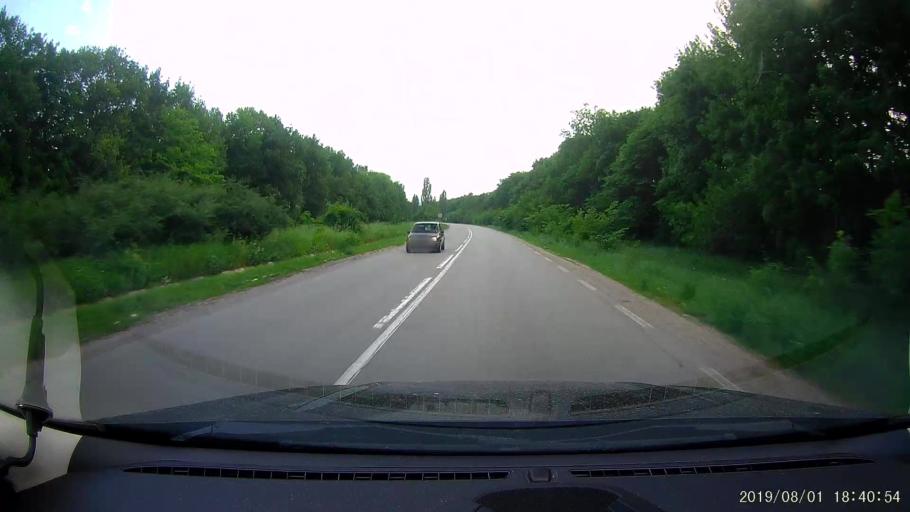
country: BG
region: Shumen
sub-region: Obshtina Khitrino
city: Gara Khitrino
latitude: 43.3562
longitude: 26.9216
